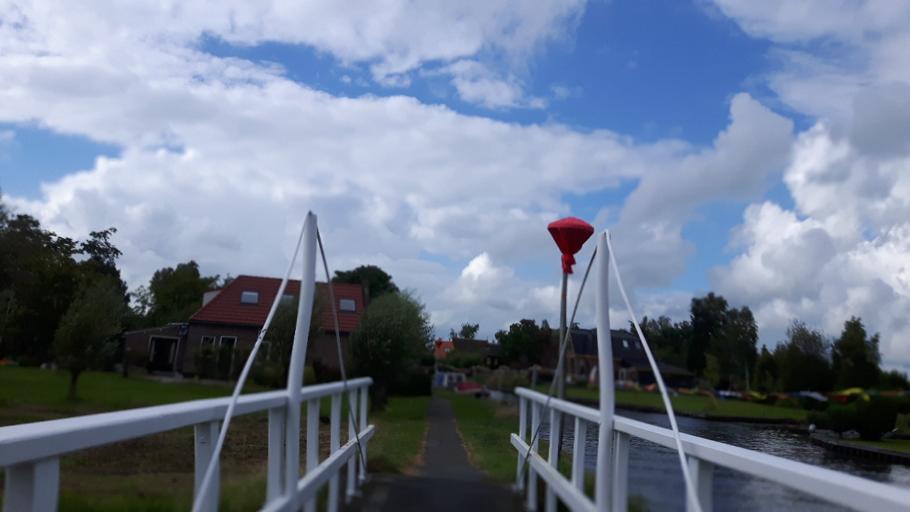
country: NL
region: Overijssel
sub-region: Gemeente Steenwijkerland
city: Blokzijl
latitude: 52.7743
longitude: 5.9593
